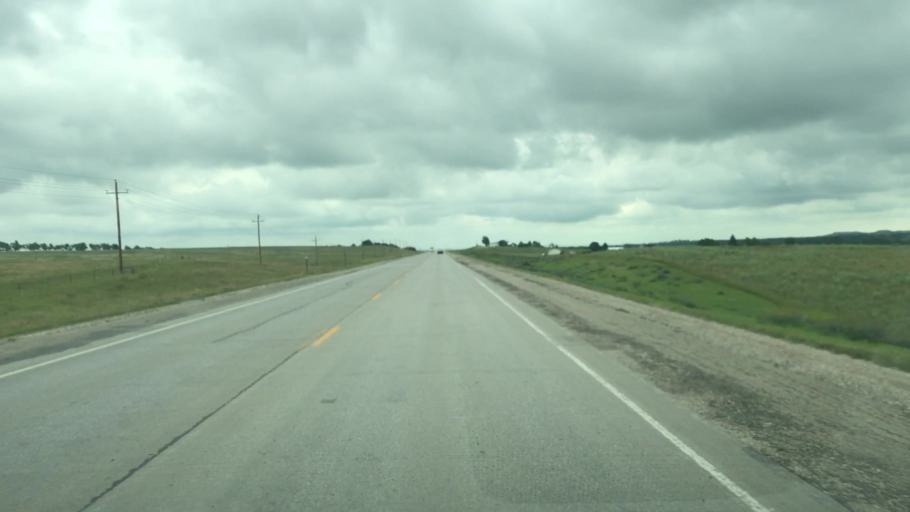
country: US
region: South Dakota
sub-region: Todd County
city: Mission
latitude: 43.3029
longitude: -100.7053
